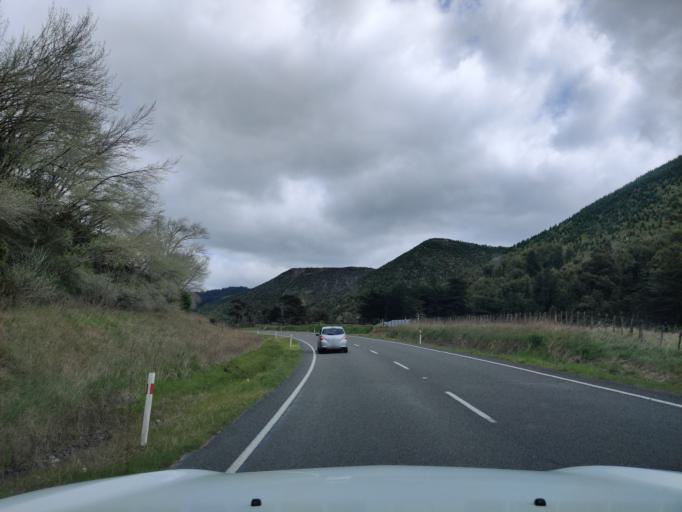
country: NZ
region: Manawatu-Wanganui
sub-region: Wanganui District
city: Wanganui
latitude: -39.8141
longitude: 175.1853
